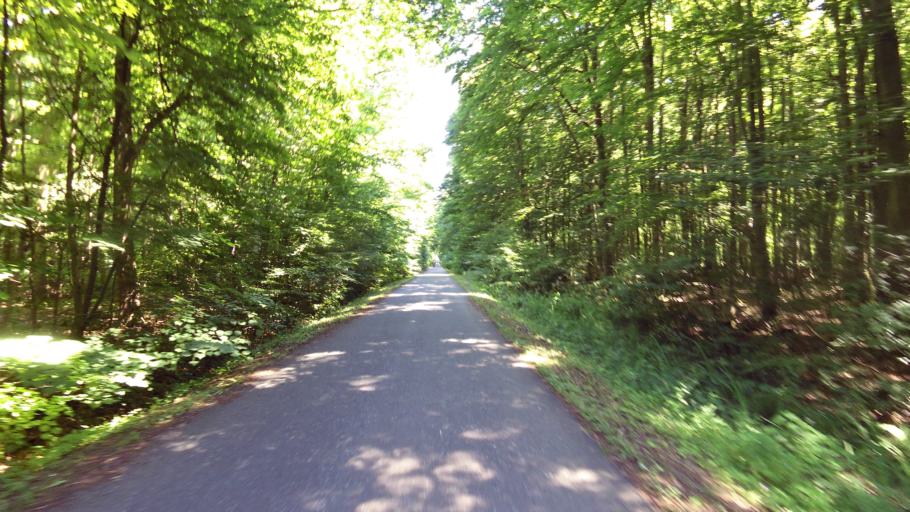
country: DE
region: North Rhine-Westphalia
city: Meckenheim
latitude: 50.6584
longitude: 7.0442
